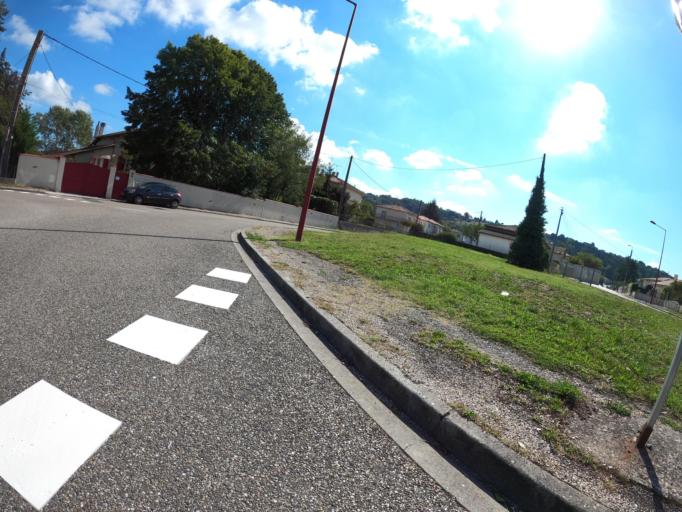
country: FR
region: Aquitaine
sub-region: Departement du Lot-et-Garonne
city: Pujols
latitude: 44.3936
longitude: 0.6935
